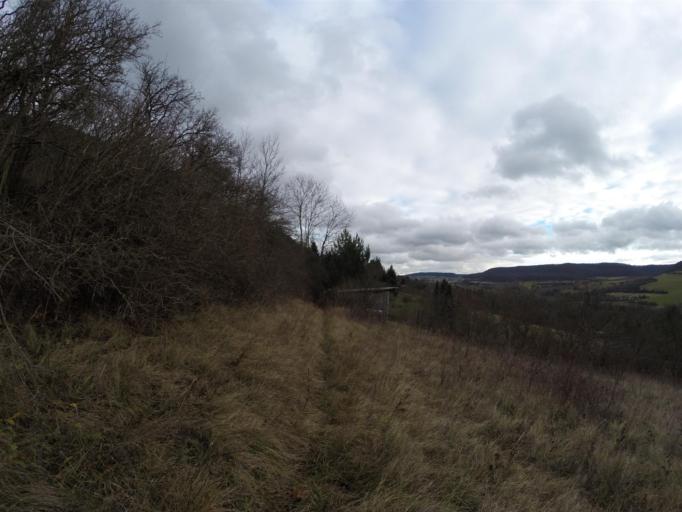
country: DE
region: Thuringia
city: Jena
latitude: 50.9360
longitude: 11.6294
